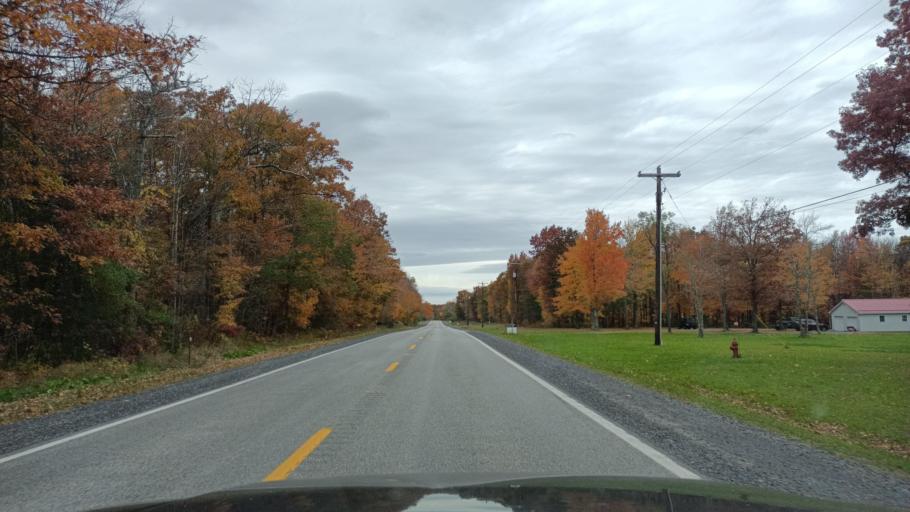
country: US
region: Maryland
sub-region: Garrett County
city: Mountain Lake Park
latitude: 39.2531
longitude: -79.2283
